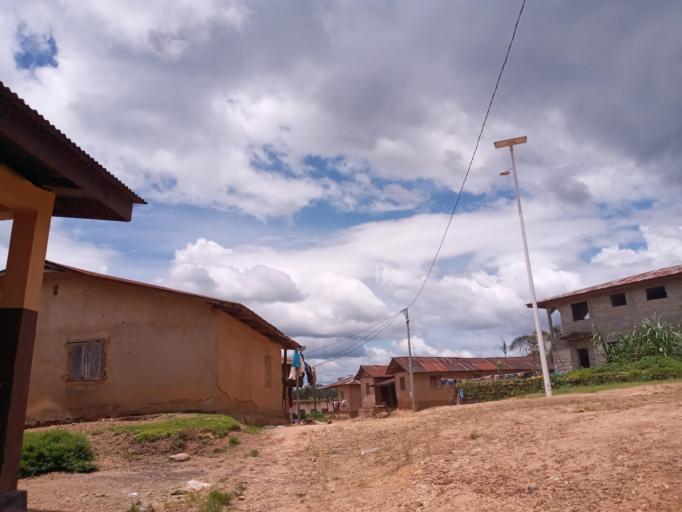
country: SL
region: Eastern Province
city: Tombu
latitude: 8.6247
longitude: -10.8228
